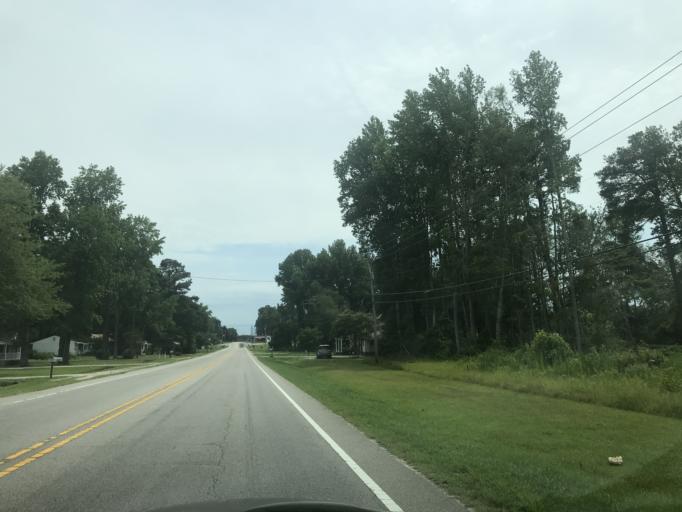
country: US
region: North Carolina
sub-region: Vance County
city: South Henderson
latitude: 36.2808
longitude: -78.4058
